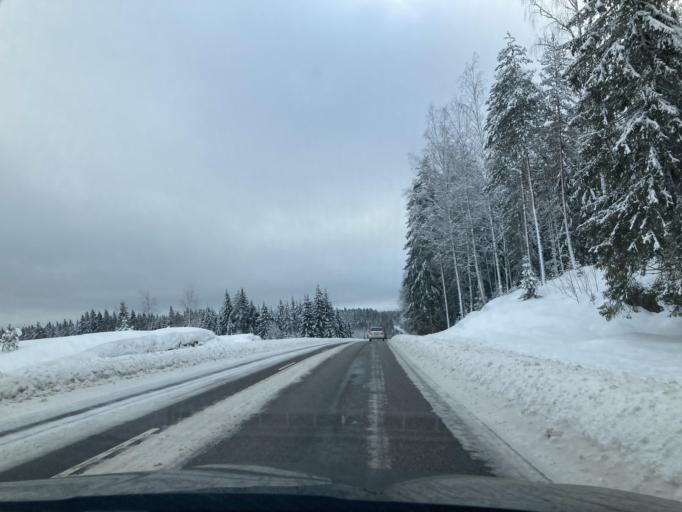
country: FI
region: Central Finland
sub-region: Jaemsae
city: Kuhmoinen
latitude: 61.6104
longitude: 25.2591
